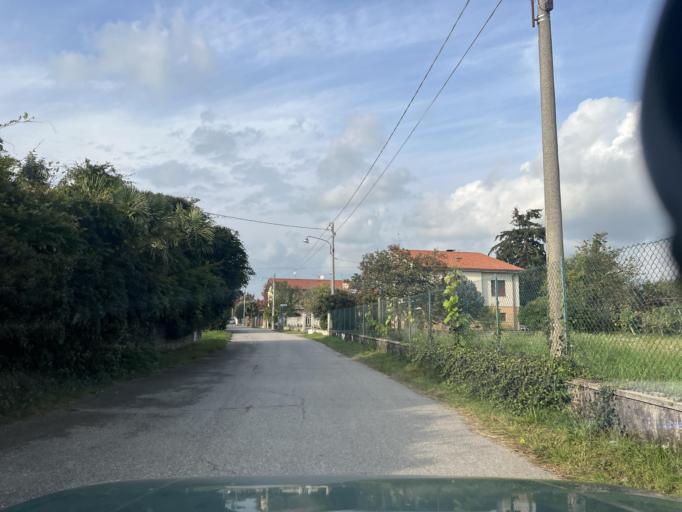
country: IT
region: Friuli Venezia Giulia
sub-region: Provincia di Gorizia
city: Mossa
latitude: 45.9335
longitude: 13.5558
